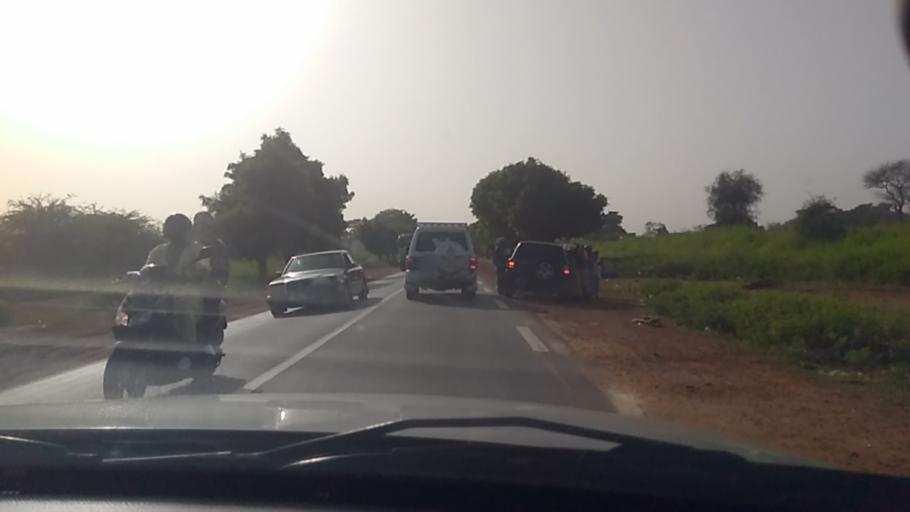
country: SN
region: Diourbel
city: Diourbel
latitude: 14.6672
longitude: -16.3284
